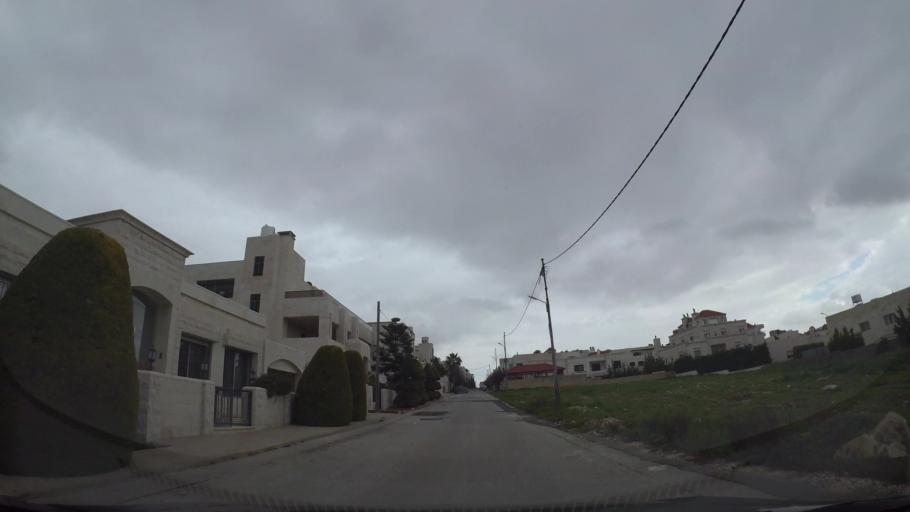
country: JO
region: Amman
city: Wadi as Sir
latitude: 31.9632
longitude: 35.8242
